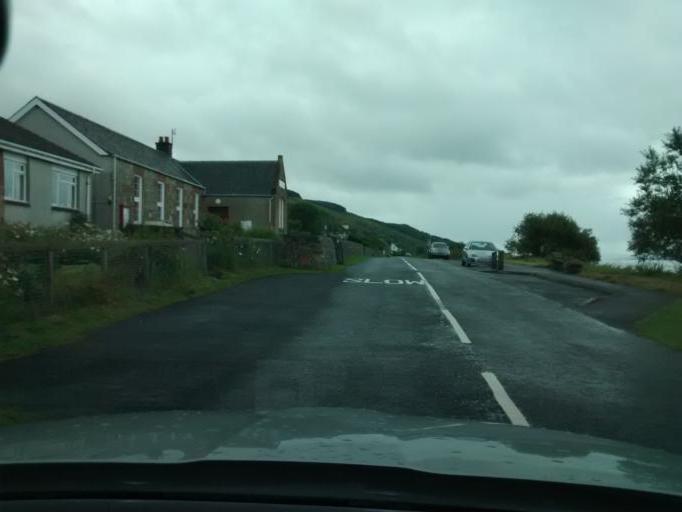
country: GB
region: Scotland
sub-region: North Ayrshire
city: Isle of Arran
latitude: 55.6476
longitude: -5.3818
